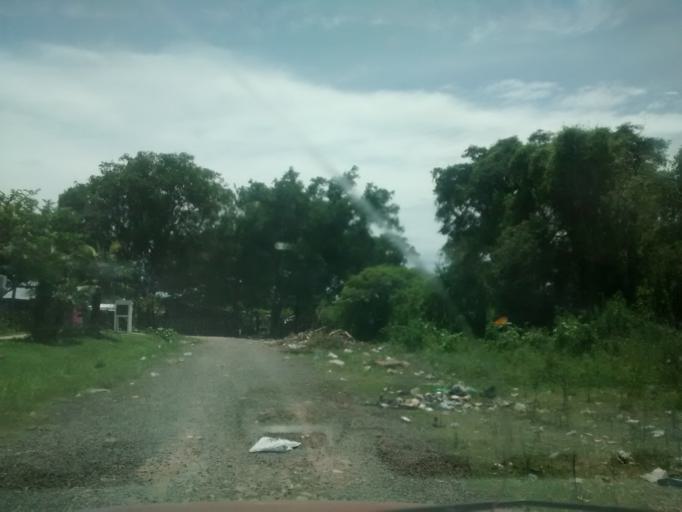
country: AR
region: Chaco
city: Resistencia
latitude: -27.4350
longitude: -58.9747
